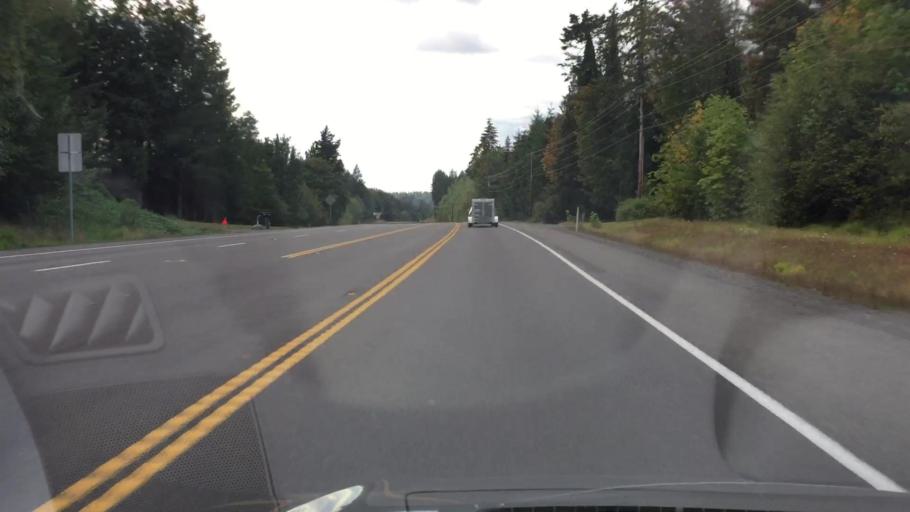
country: US
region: Washington
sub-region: Lewis County
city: Napavine
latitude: 46.5258
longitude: -122.5964
